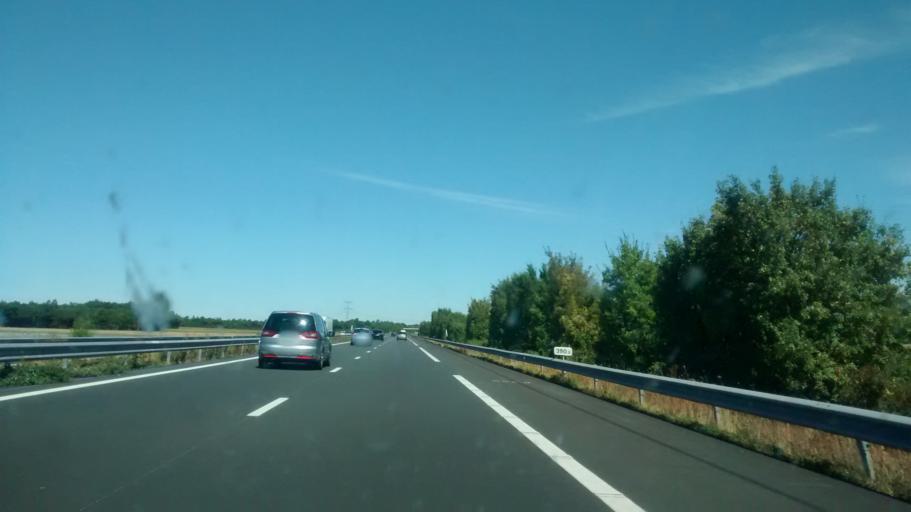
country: FR
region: Poitou-Charentes
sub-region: Departement des Deux-Sevres
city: Beauvoir-sur-Niort
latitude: 46.1601
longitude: -0.5150
